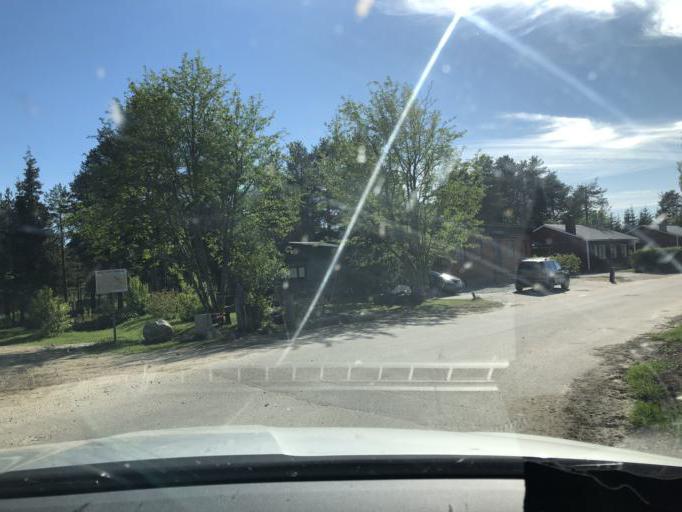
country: SE
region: Norrbotten
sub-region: Jokkmokks Kommun
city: Jokkmokk
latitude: 66.6027
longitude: 19.8286
